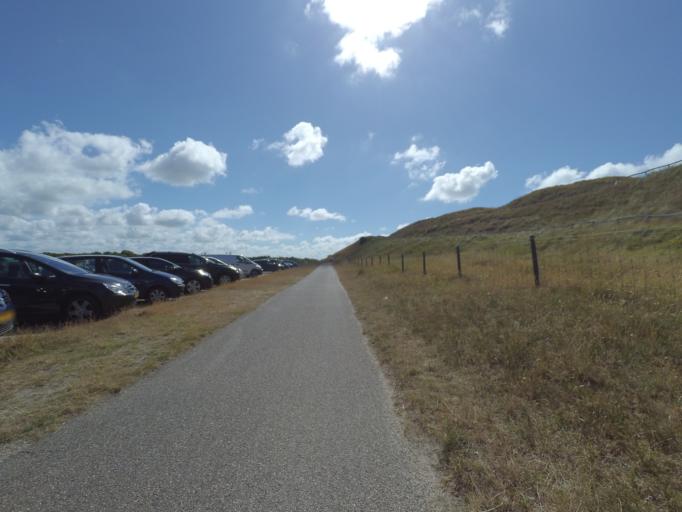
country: NL
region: North Holland
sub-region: Gemeente Texel
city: Den Burg
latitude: 53.1308
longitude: 4.8165
